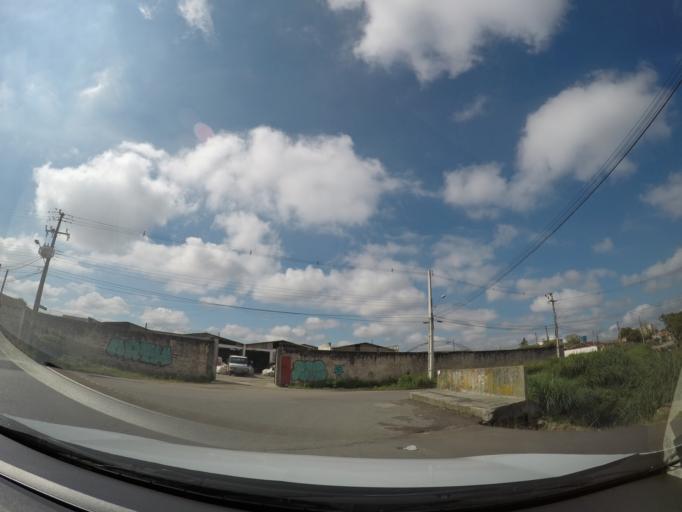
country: BR
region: Parana
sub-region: Sao Jose Dos Pinhais
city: Sao Jose dos Pinhais
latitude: -25.4966
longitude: -49.2225
